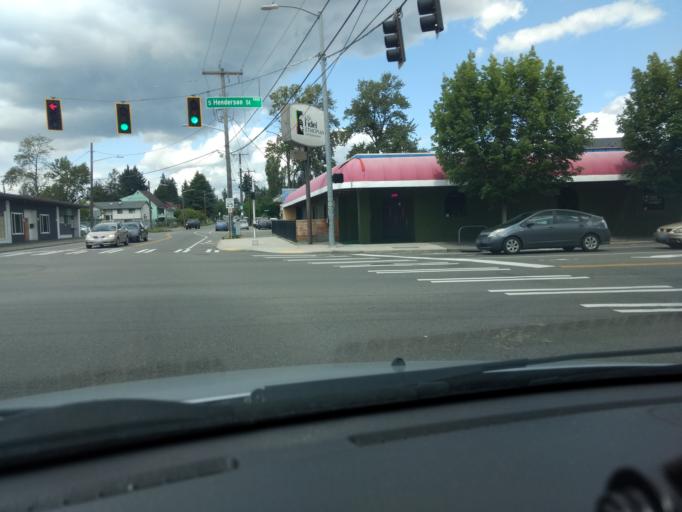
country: US
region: Washington
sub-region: King County
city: Riverton
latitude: 47.5232
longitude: -122.2763
